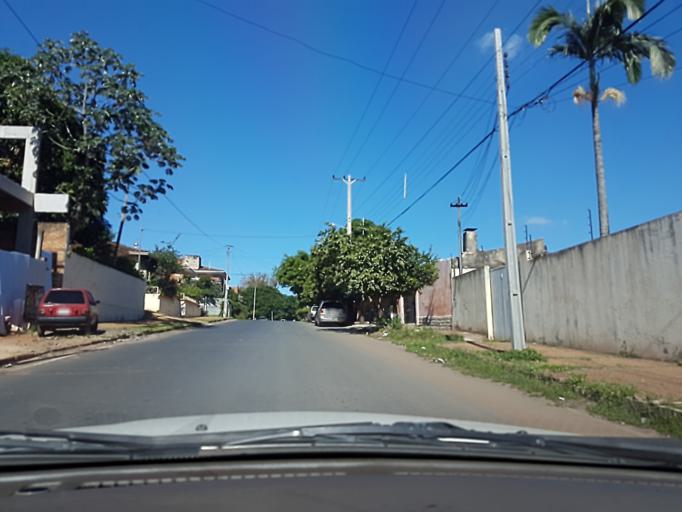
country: PY
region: Central
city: Lambare
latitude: -25.3219
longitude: -57.5881
